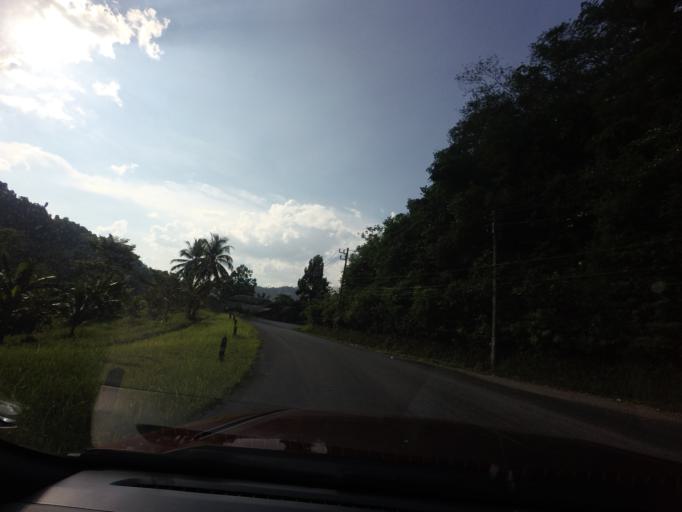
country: TH
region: Yala
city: Than To
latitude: 6.1513
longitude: 101.2811
